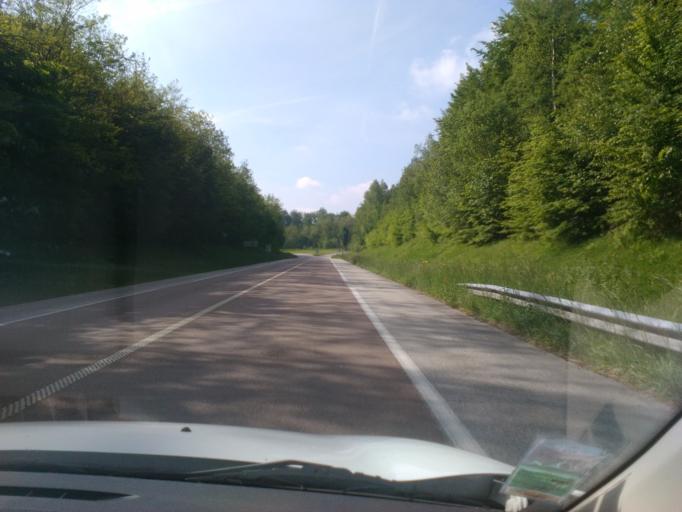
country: FR
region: Lorraine
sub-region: Departement des Vosges
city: Les Forges
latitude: 48.1934
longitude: 6.3998
